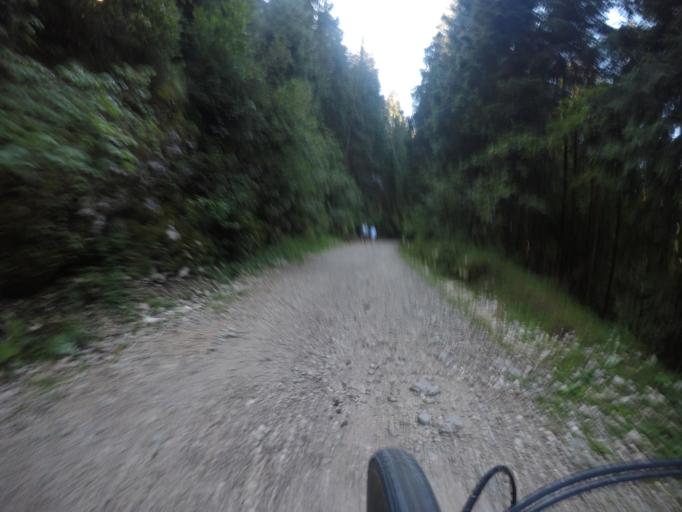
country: IT
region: Veneto
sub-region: Provincia di Vicenza
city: Canove di Roana
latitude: 45.8515
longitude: 11.4771
